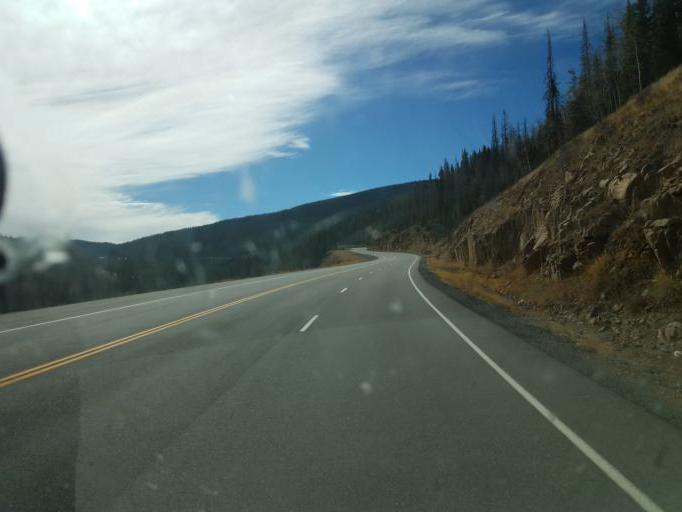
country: US
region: Colorado
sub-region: Archuleta County
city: Pagosa Springs
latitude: 37.5171
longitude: -106.7720
